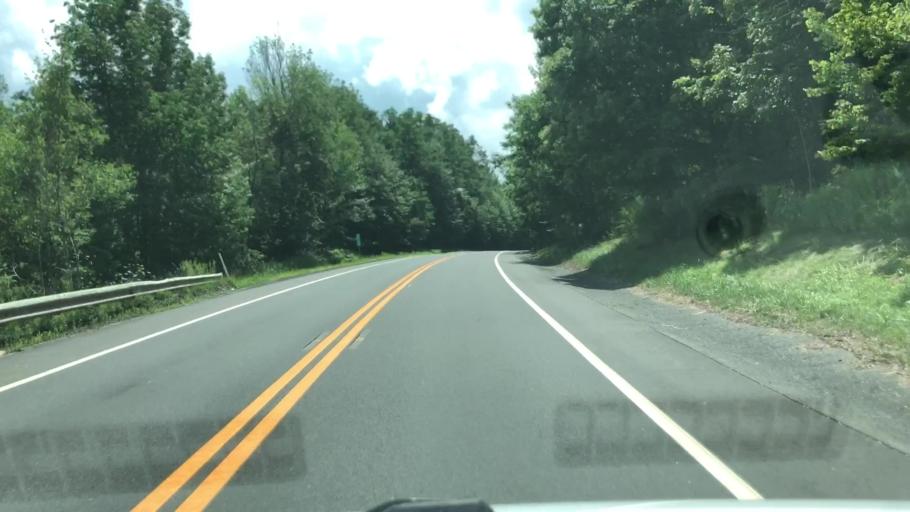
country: US
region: Massachusetts
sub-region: Franklin County
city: Ashfield
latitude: 42.5179
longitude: -72.8066
